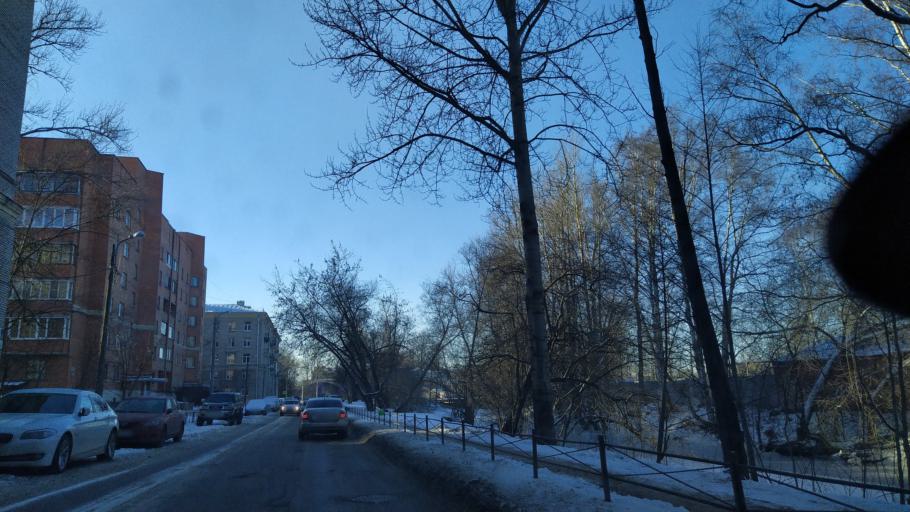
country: RU
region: St.-Petersburg
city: Novaya Derevnya
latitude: 59.9894
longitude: 30.2917
